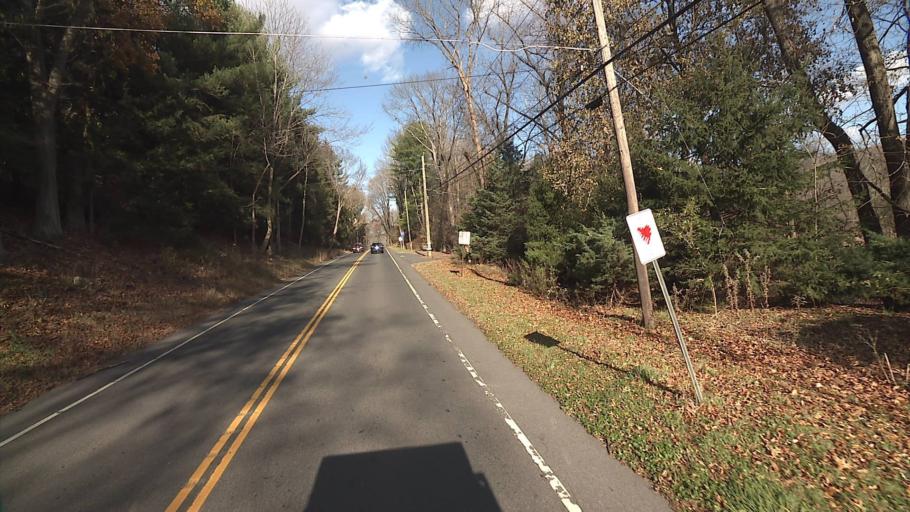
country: US
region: Connecticut
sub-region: Fairfield County
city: Bethel
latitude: 41.3371
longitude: -73.4171
